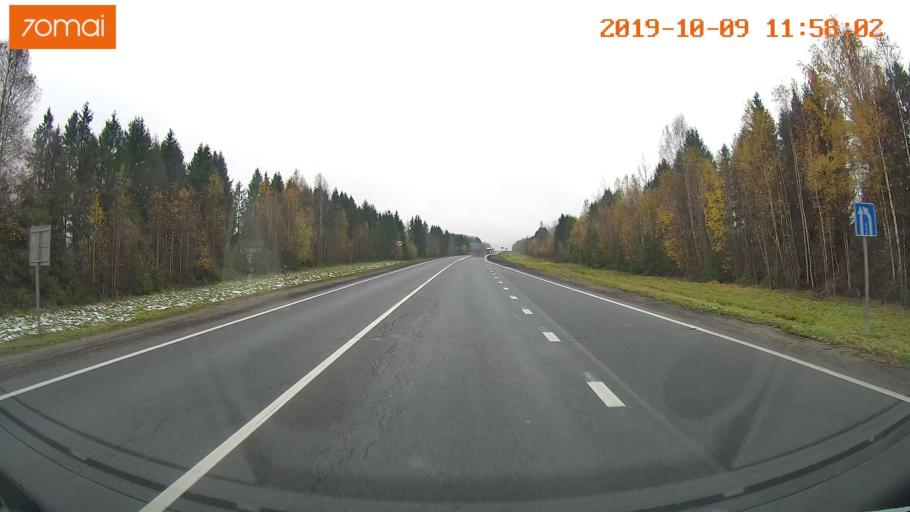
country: RU
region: Vologda
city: Gryazovets
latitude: 58.7239
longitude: 40.2958
